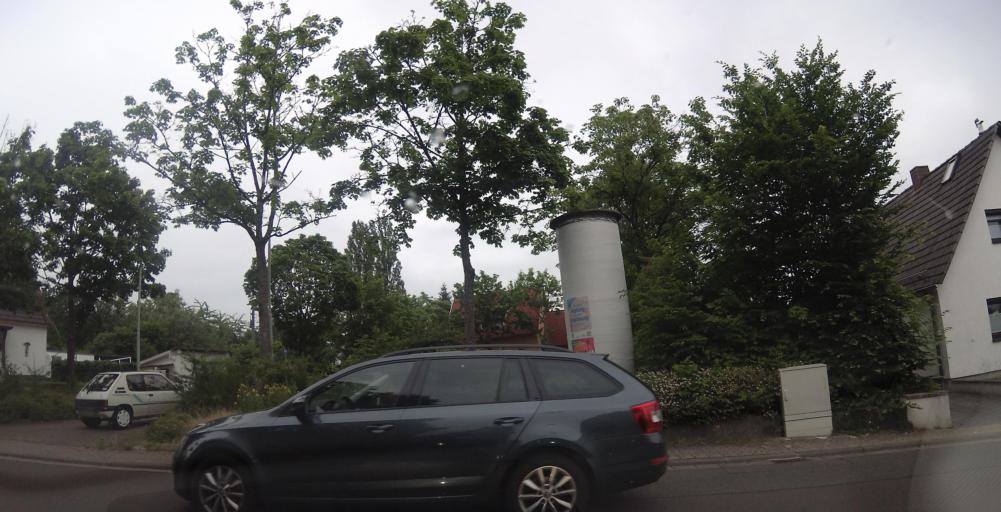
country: DE
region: Saarland
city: Saarbrucken
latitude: 49.2550
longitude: 6.9594
